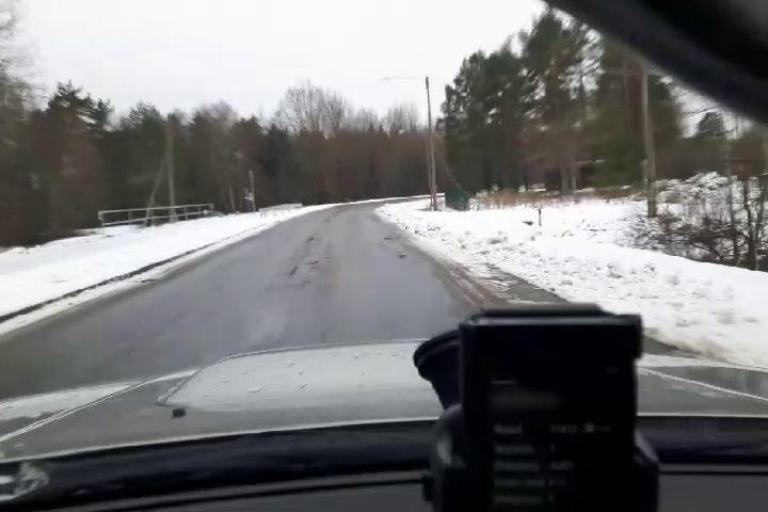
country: EE
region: Harju
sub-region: Harku vald
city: Tabasalu
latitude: 59.4315
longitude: 24.4889
